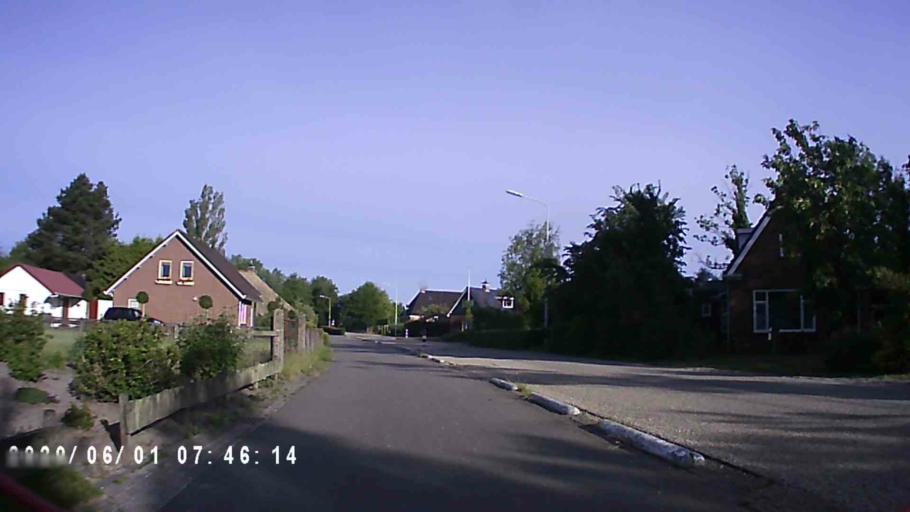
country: NL
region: Friesland
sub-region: Gemeente Dantumadiel
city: Rinsumageast
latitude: 53.2946
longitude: 5.9586
